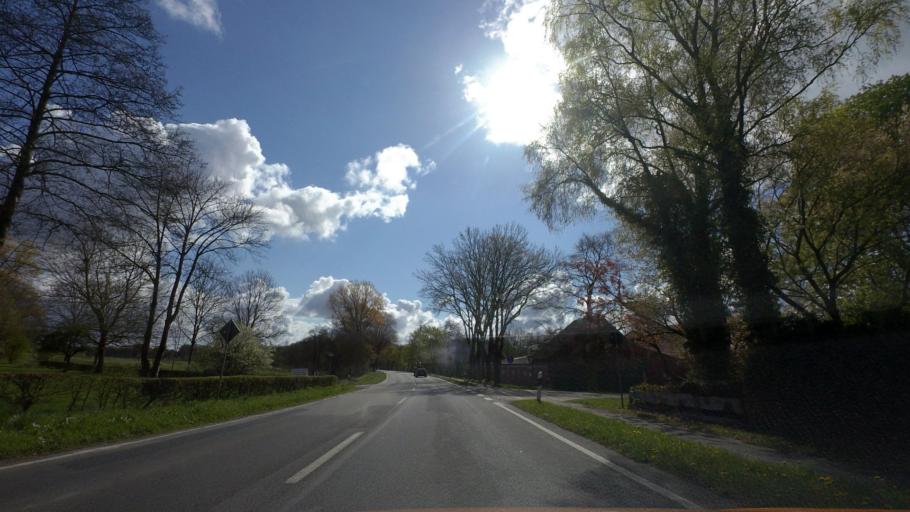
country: DE
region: Lower Saxony
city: Ganderkesee
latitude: 53.0459
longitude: 8.5039
